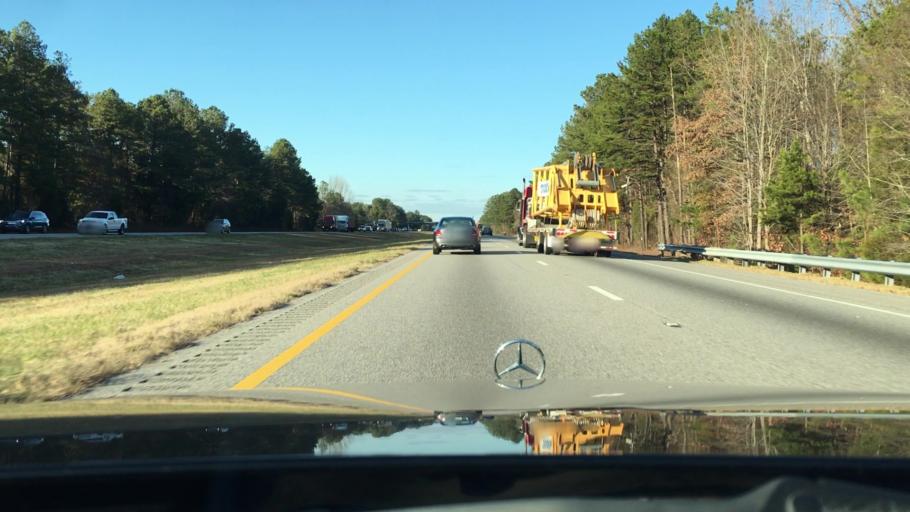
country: US
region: South Carolina
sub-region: Chester County
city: Great Falls
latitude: 34.6725
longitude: -81.0290
